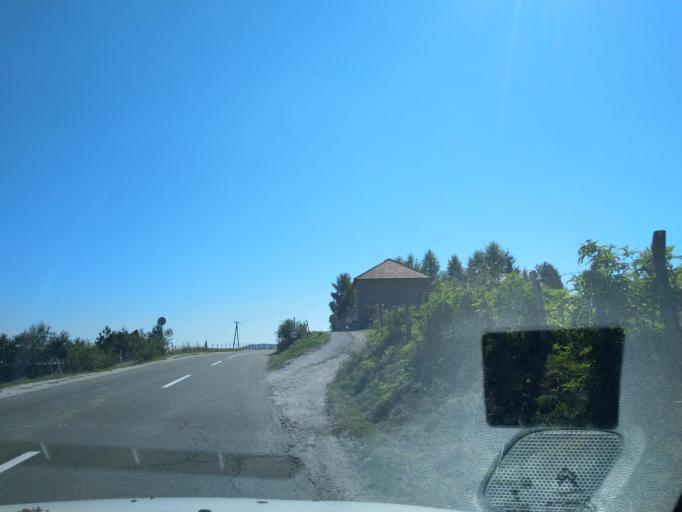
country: RS
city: Sokolovica
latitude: 43.2732
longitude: 20.2232
